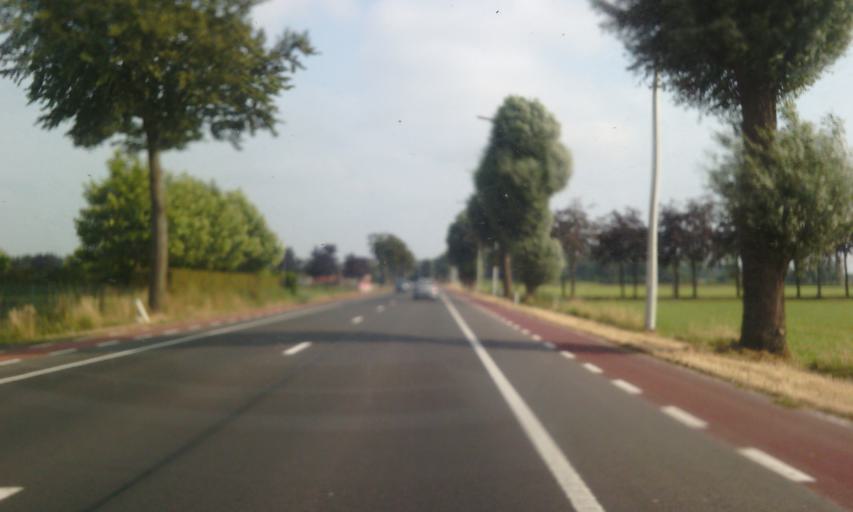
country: BE
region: Flanders
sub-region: Provincie Oost-Vlaanderen
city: Waarschoot
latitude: 51.1627
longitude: 3.5883
